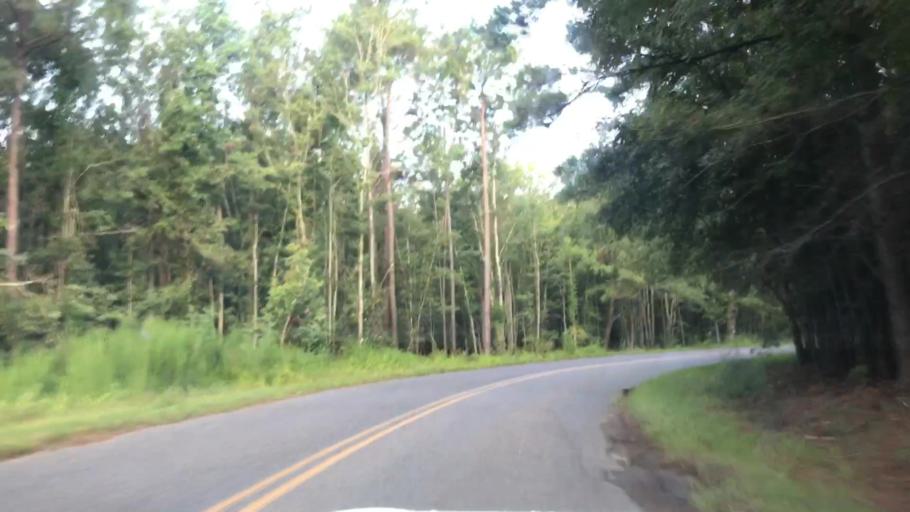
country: US
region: South Carolina
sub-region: Charleston County
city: Shell Point
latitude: 32.8152
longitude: -80.0884
